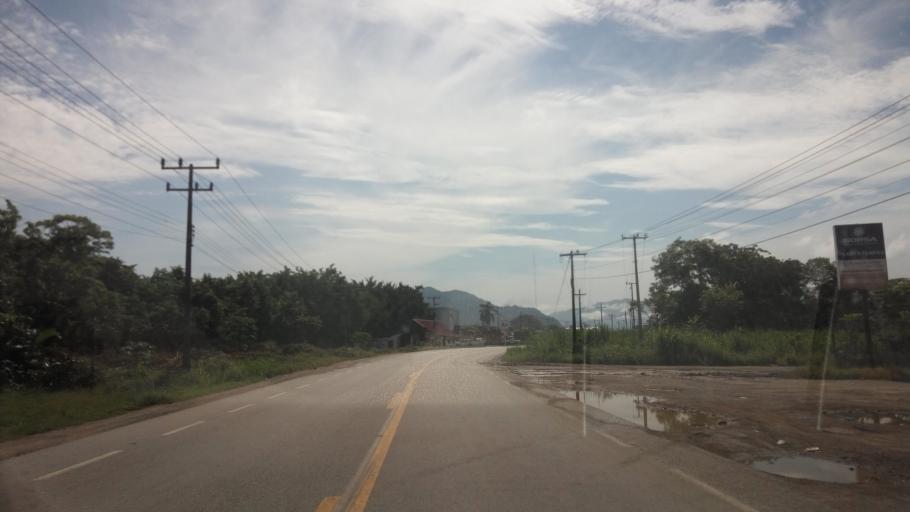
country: MX
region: Tabasco
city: Teapa
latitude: 17.5809
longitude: -92.9650
